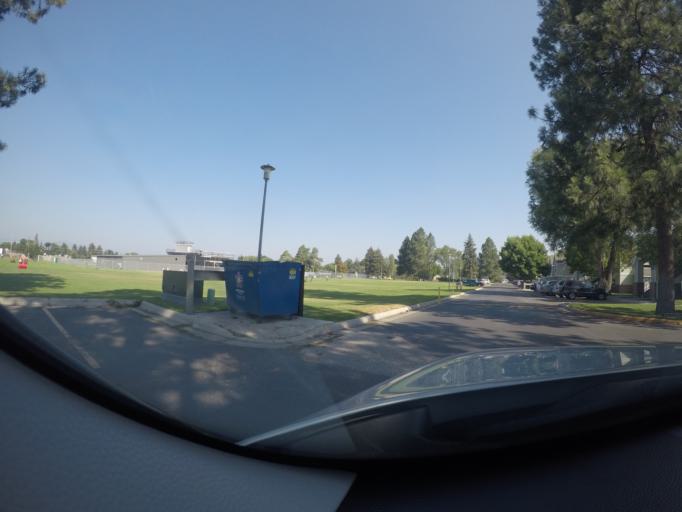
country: US
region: Montana
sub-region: Missoula County
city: Missoula
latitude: 46.8472
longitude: -113.9933
